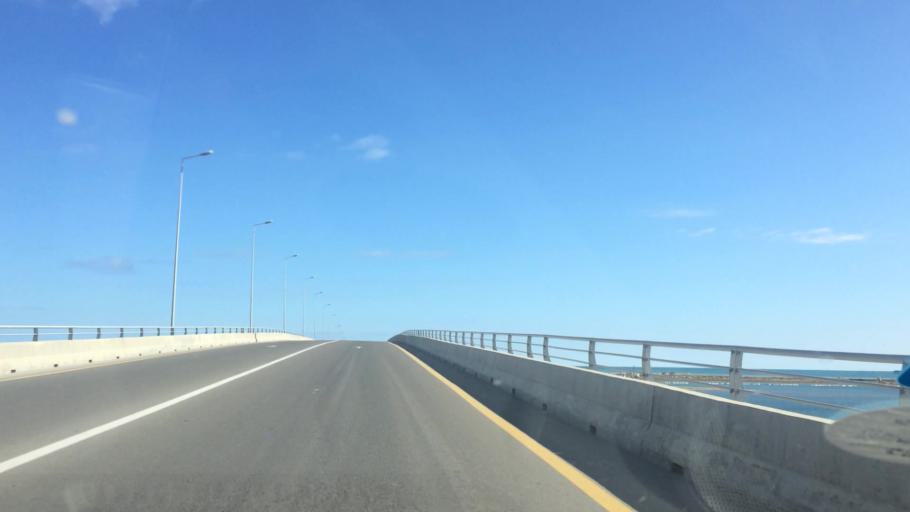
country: AZ
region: Baki
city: Pirallahi
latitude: 40.4064
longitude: 50.3462
